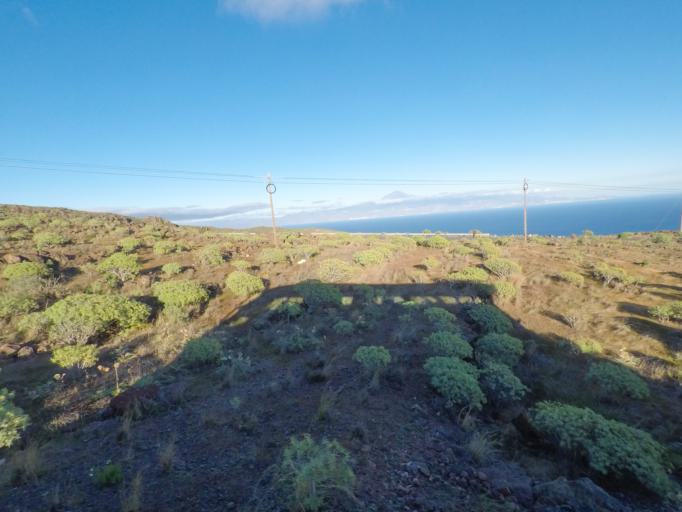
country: ES
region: Canary Islands
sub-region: Provincia de Santa Cruz de Tenerife
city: San Sebastian de la Gomera
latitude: 28.0876
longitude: -17.1469
